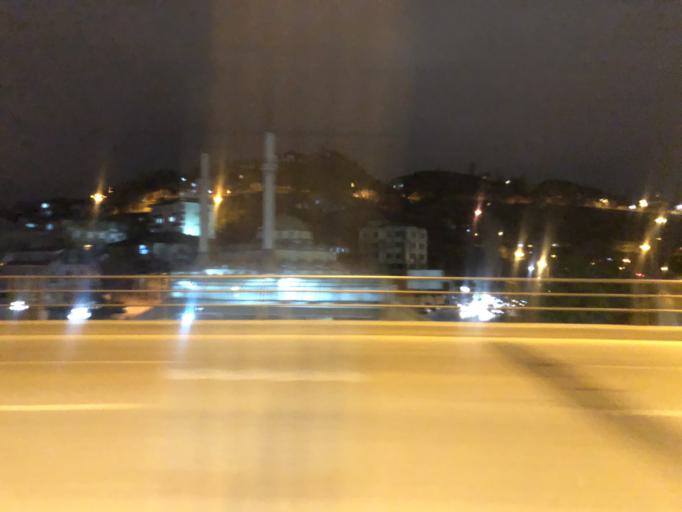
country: TR
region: Ankara
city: Ankara
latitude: 39.9511
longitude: 32.8586
